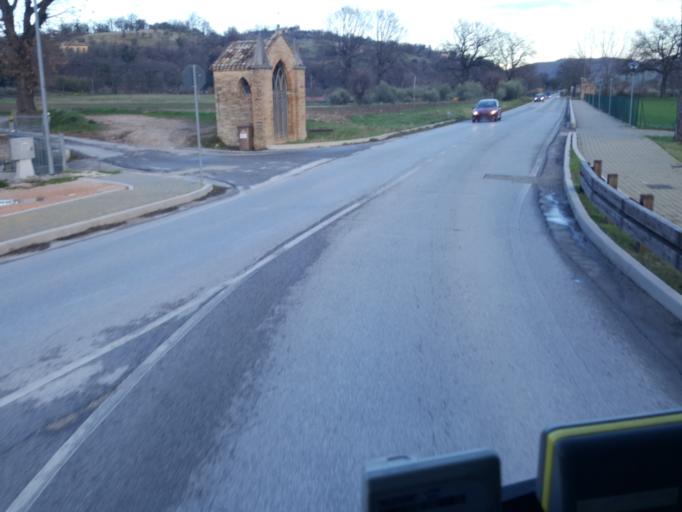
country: IT
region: The Marches
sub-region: Provincia di Macerata
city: San Severino Marche
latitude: 43.2352
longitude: 13.1936
